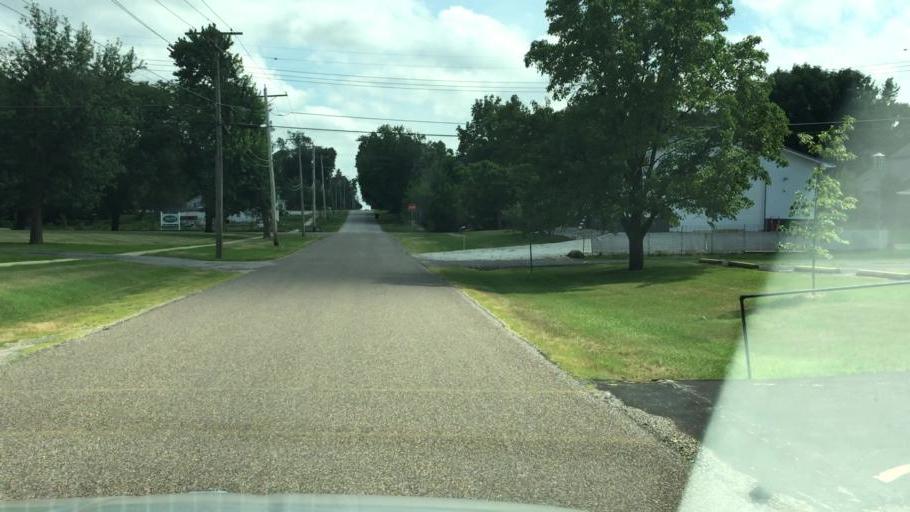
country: US
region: Illinois
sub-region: Hancock County
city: Carthage
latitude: 40.4133
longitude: -91.1381
